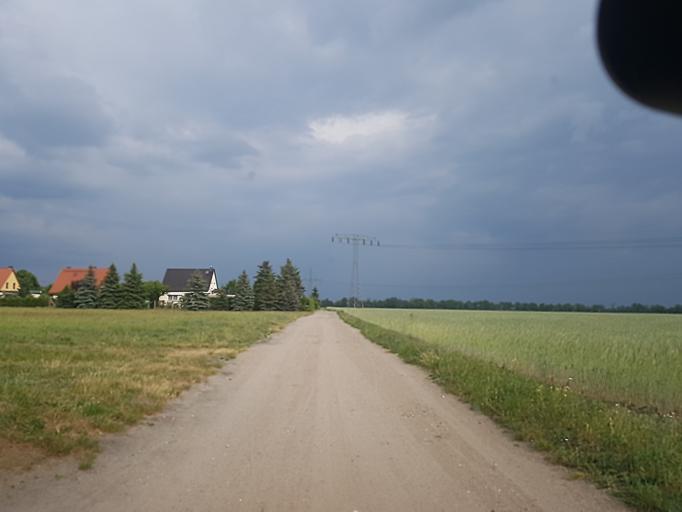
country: DE
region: Saxony-Anhalt
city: Muhlanger
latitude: 51.8504
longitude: 12.7486
